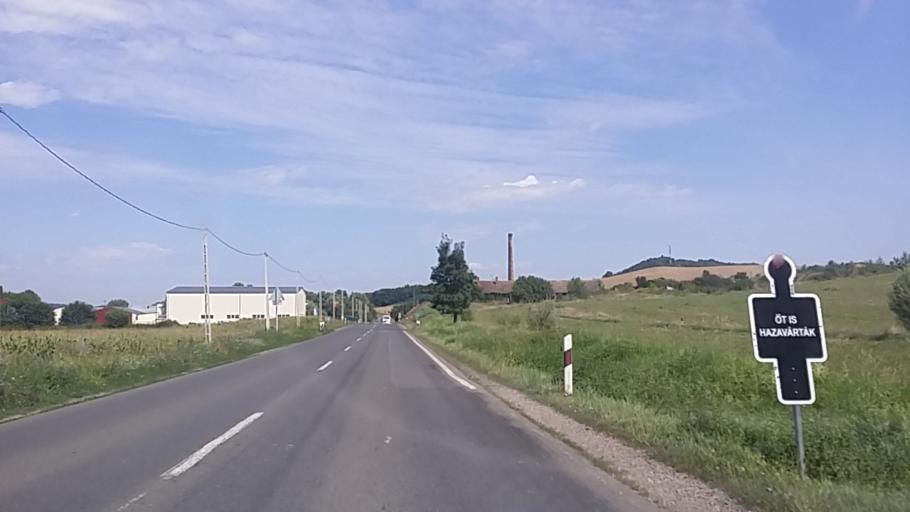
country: HU
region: Baranya
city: Sasd
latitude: 46.2412
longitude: 18.1208
